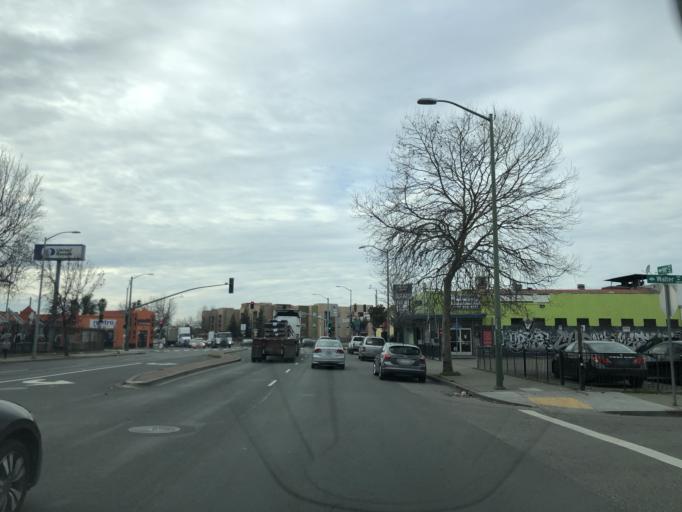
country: US
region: California
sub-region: Alameda County
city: San Leandro
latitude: 37.7371
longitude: -122.1826
